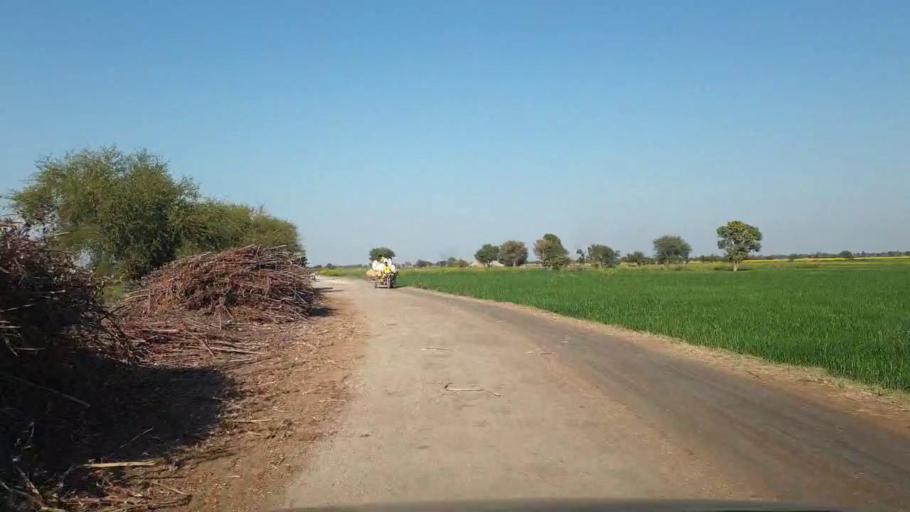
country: PK
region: Sindh
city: Shahpur Chakar
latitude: 26.1599
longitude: 68.6844
